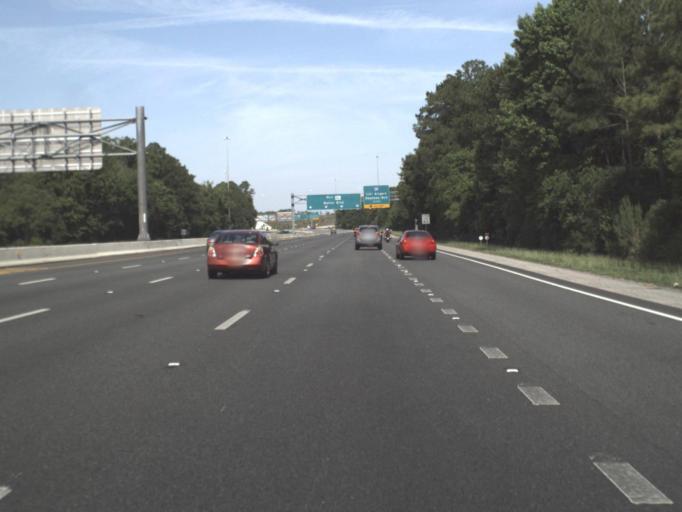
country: US
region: Florida
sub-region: Duval County
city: Jacksonville Beach
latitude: 30.2532
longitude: -81.5034
